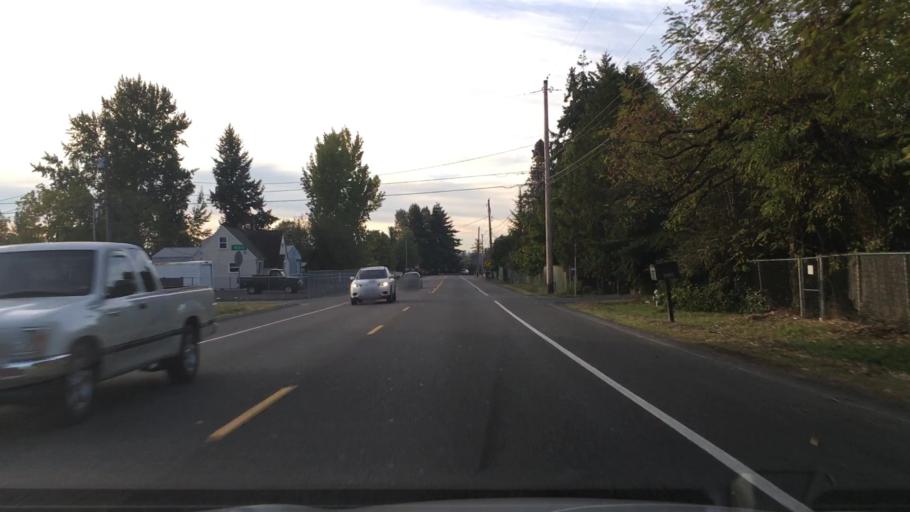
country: US
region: Washington
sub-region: Pierce County
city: Midland
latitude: 47.1747
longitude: -122.4064
